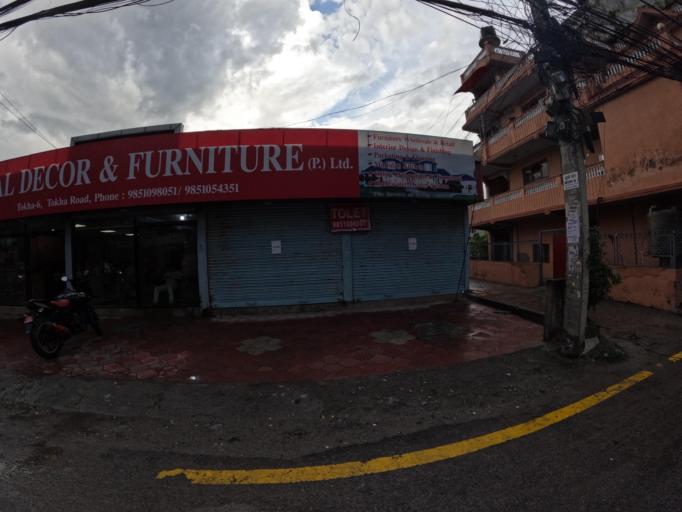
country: NP
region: Central Region
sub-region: Bagmati Zone
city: Kathmandu
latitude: 27.7499
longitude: 85.3253
